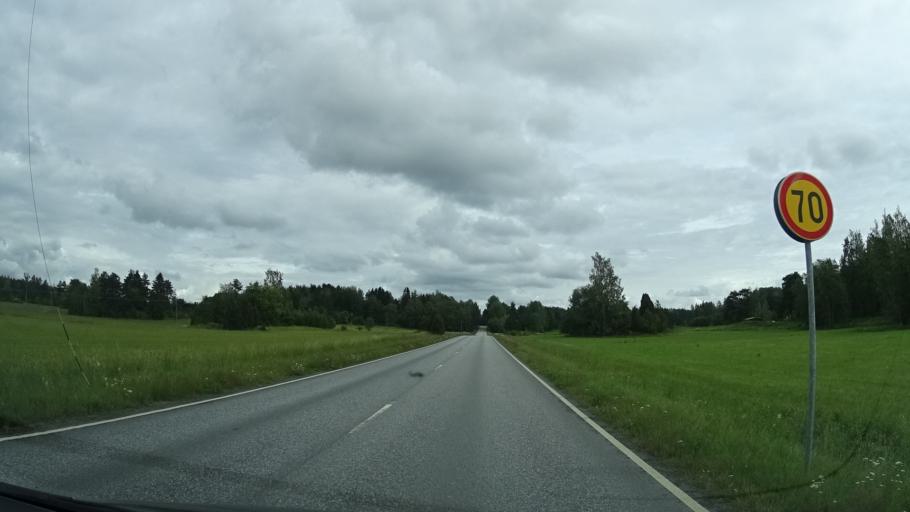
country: FI
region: Pirkanmaa
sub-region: Etelae-Pirkanmaa
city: Urjala
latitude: 61.0874
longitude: 23.4677
